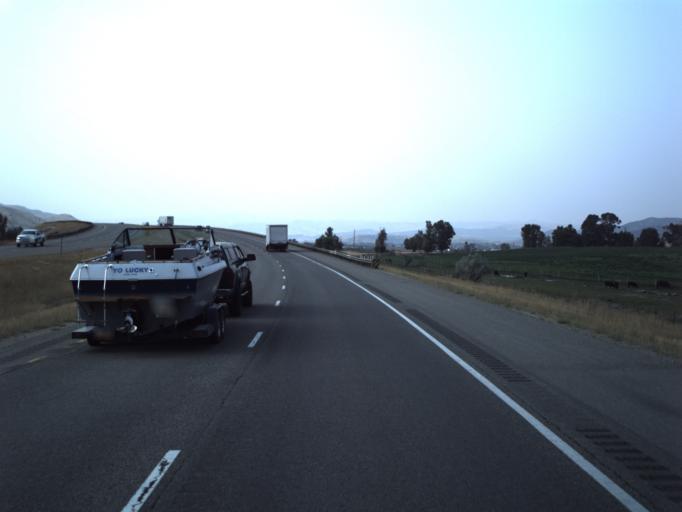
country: US
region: Utah
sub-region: Summit County
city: Coalville
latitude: 40.8430
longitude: -111.3871
